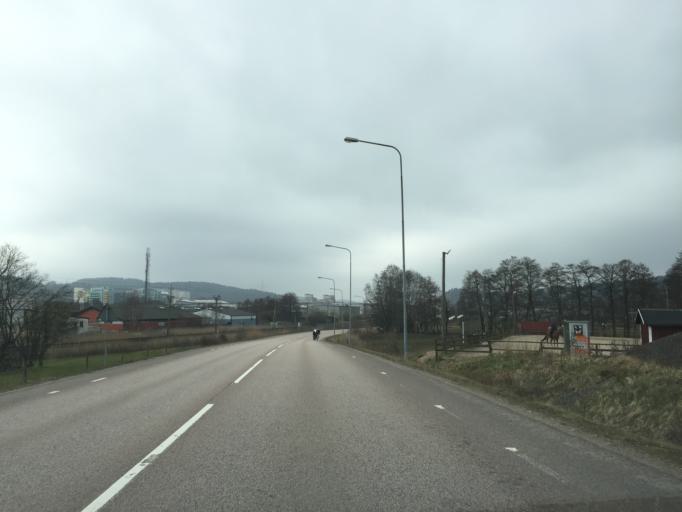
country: SE
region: Vaestra Goetaland
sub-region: Partille Kommun
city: Partille
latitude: 57.7459
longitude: 12.1305
